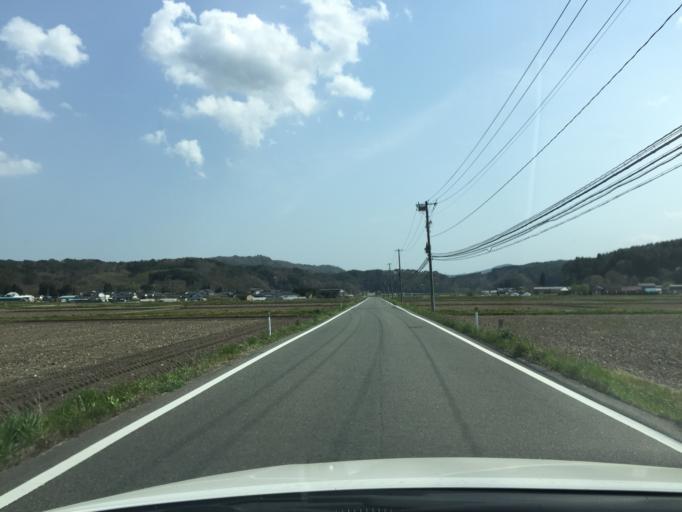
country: JP
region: Fukushima
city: Namie
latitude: 37.3226
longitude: 140.8352
